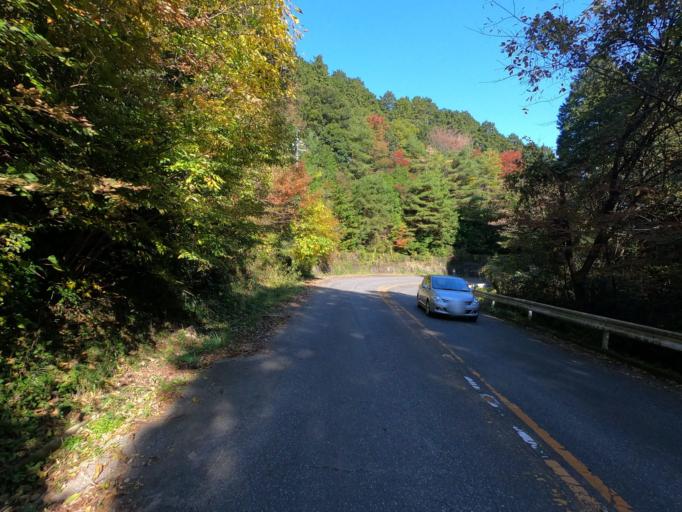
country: JP
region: Ibaraki
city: Tsukuba
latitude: 36.2179
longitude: 140.1256
